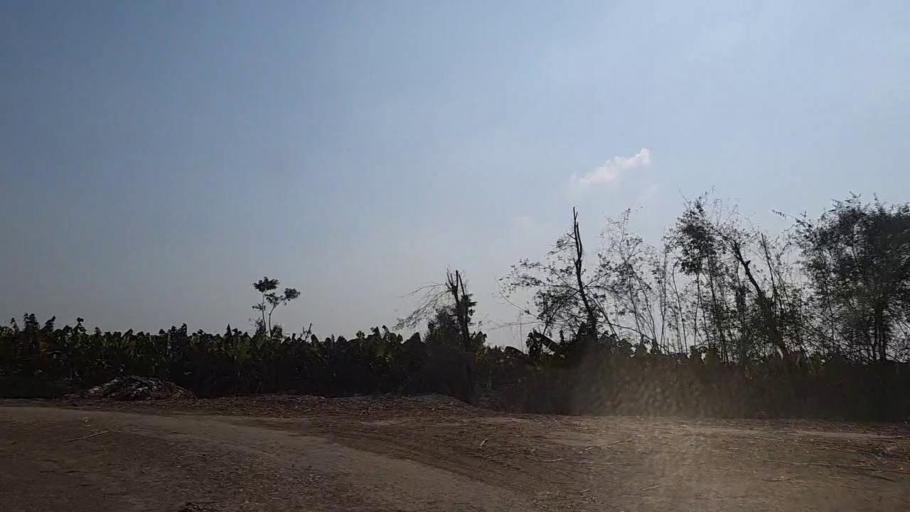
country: PK
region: Sindh
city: Daur
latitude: 26.4166
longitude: 68.2366
